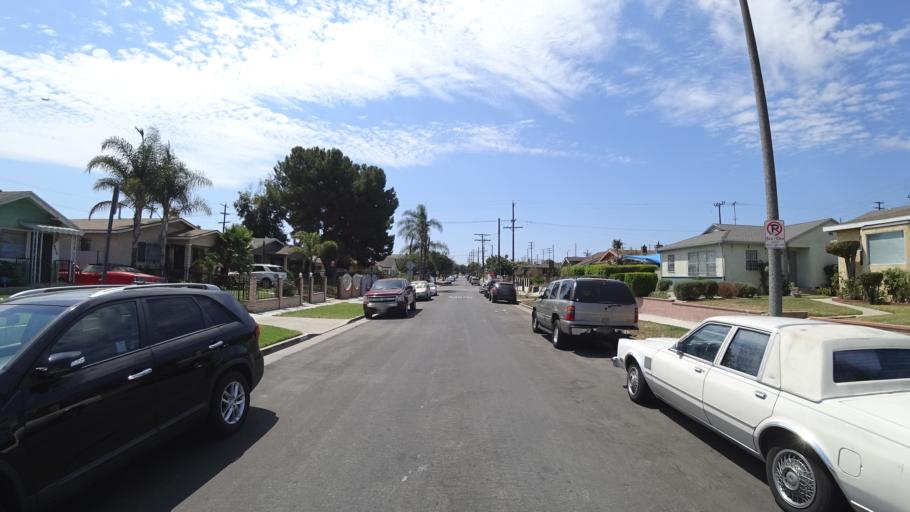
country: US
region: California
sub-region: Los Angeles County
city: Westmont
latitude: 33.9557
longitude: -118.2905
